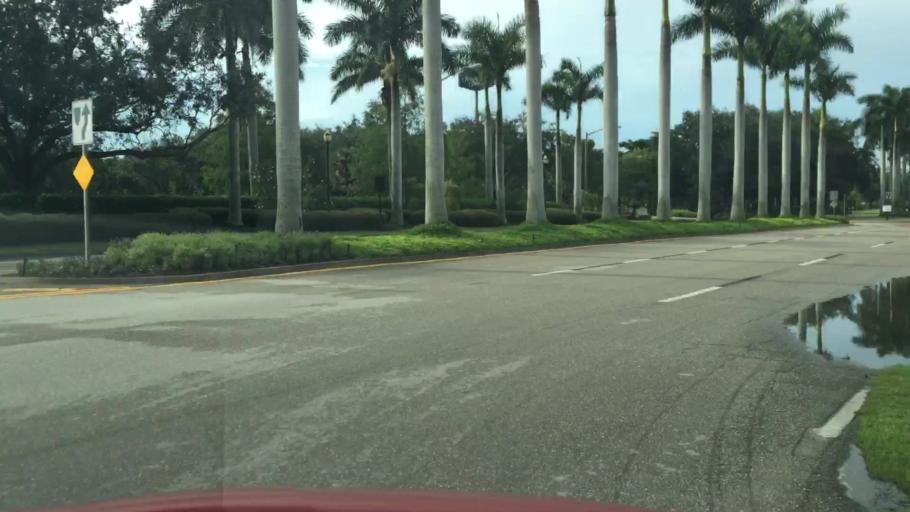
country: US
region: Florida
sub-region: Lee County
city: Gateway
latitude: 26.5475
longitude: -81.7997
